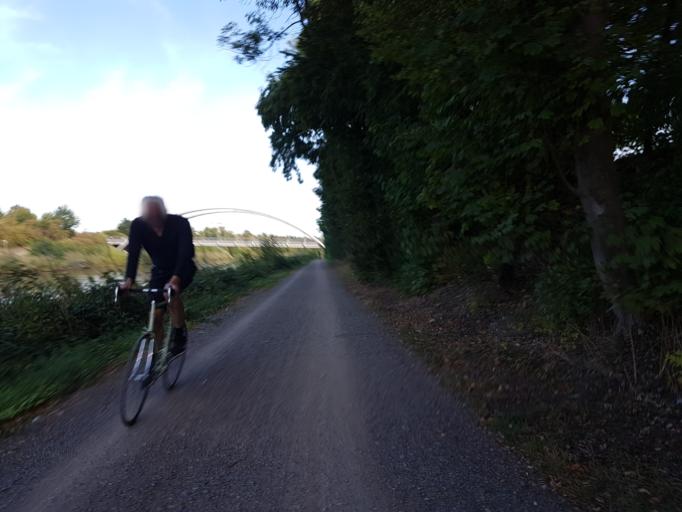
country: DE
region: Lower Saxony
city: Isernhagen Farster Bauerschaft
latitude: 52.4043
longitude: 9.8070
